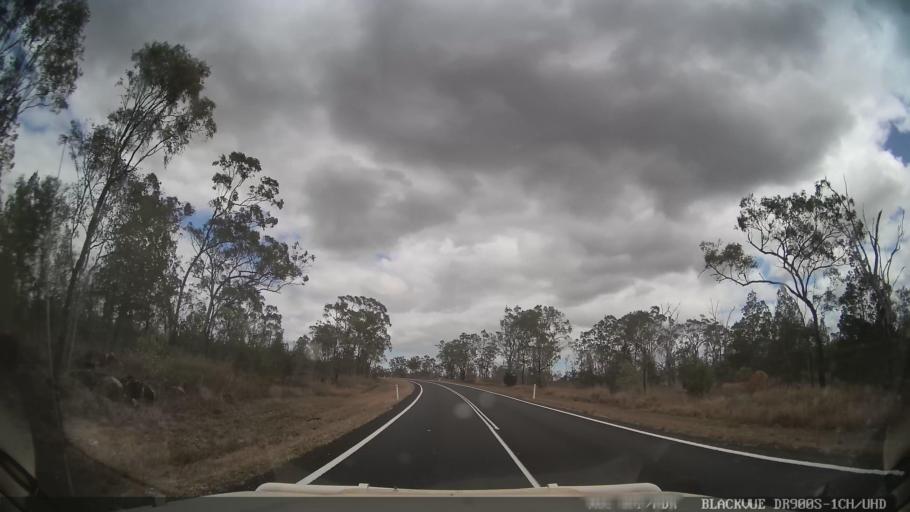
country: AU
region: Queensland
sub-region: Tablelands
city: Ravenshoe
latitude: -17.6595
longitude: 145.2444
